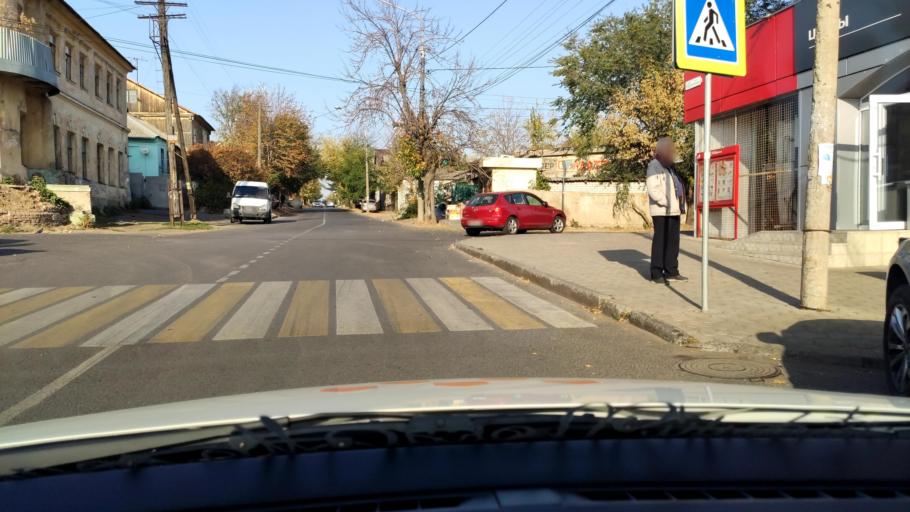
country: RU
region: Voronezj
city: Voronezh
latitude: 51.6815
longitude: 39.2208
